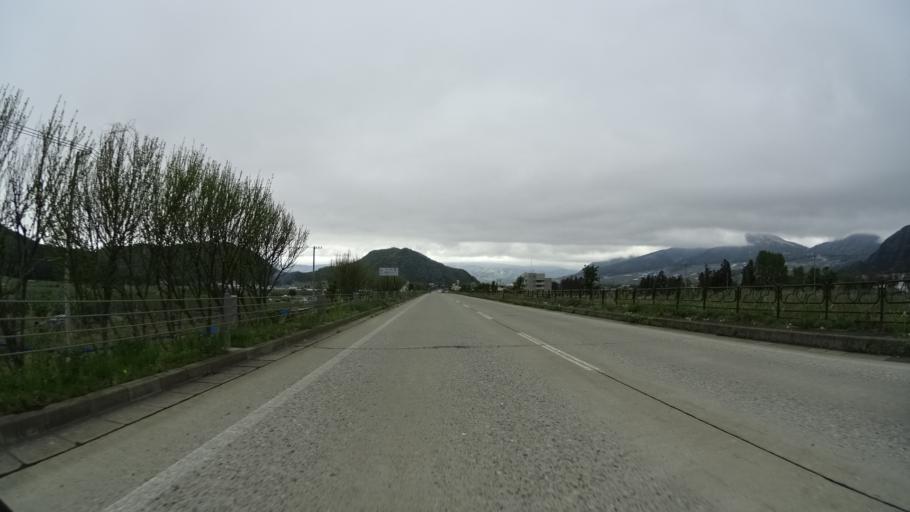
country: JP
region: Nagano
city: Nakano
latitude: 36.7386
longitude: 138.4087
